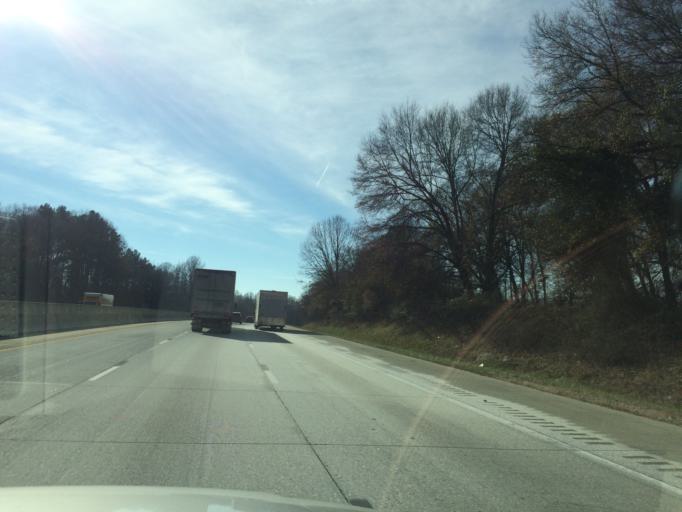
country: US
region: South Carolina
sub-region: Anderson County
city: Northlake
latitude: 34.6105
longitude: -82.6288
